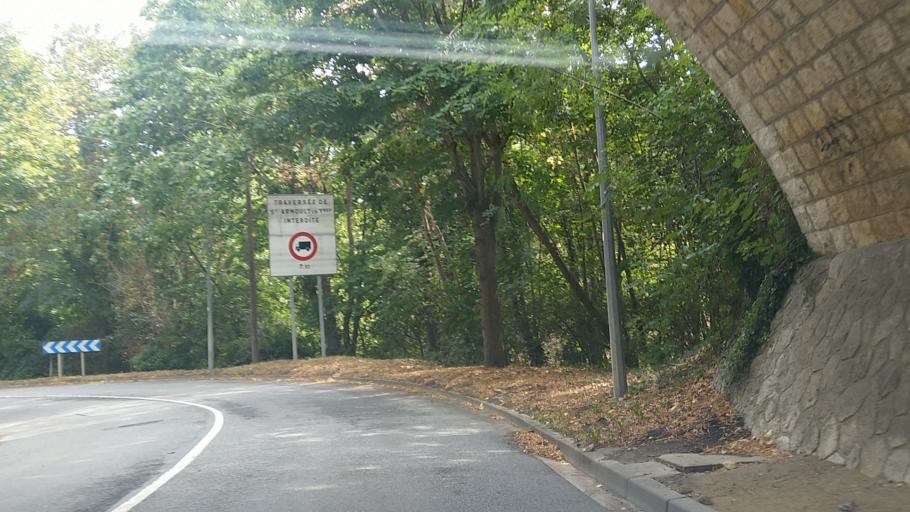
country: FR
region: Ile-de-France
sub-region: Departement des Yvelines
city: Saint-Arnoult-en-Yvelines
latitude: 48.5696
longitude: 1.9293
